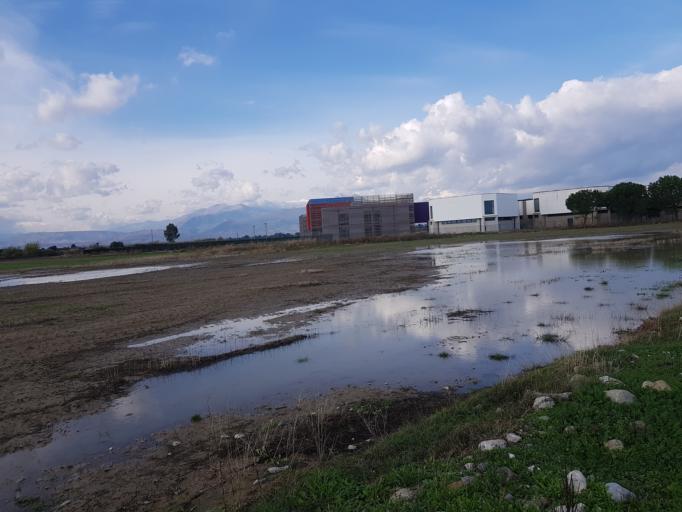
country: IT
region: Calabria
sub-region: Provincia di Cosenza
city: Sibari
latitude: 39.7248
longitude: 16.4953
